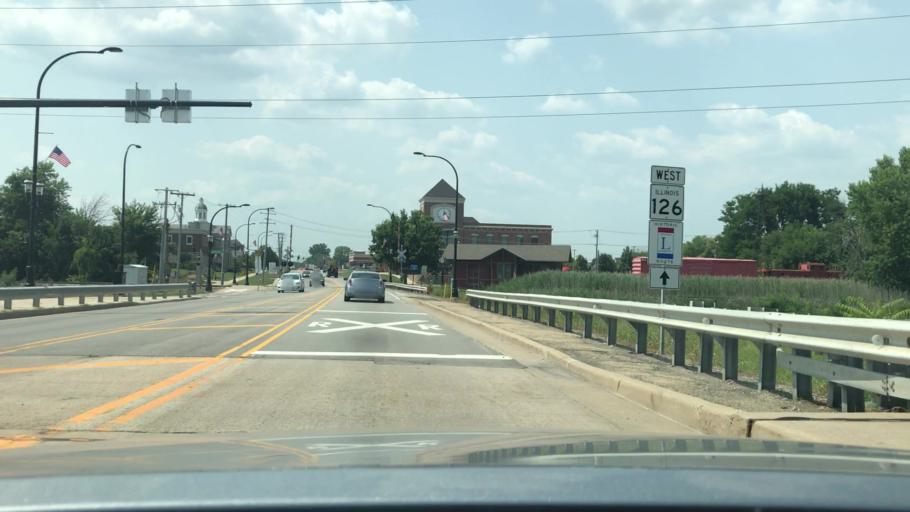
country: US
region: Illinois
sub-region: Will County
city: Plainfield
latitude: 41.6085
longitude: -88.2100
